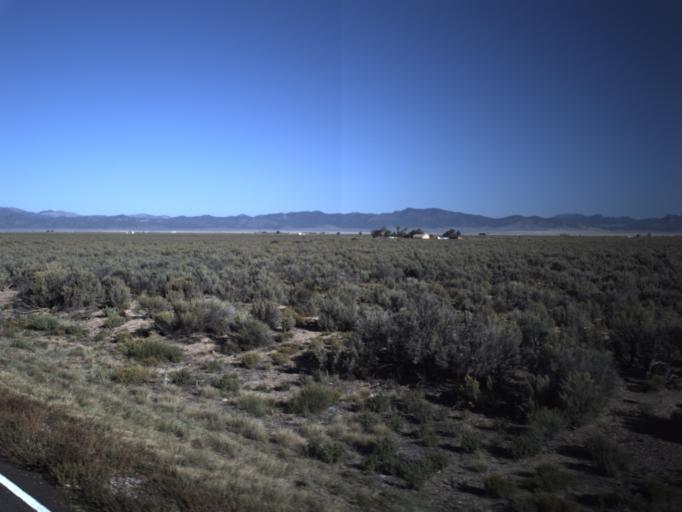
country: US
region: Utah
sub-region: Washington County
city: Enterprise
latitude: 37.7271
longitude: -113.7051
